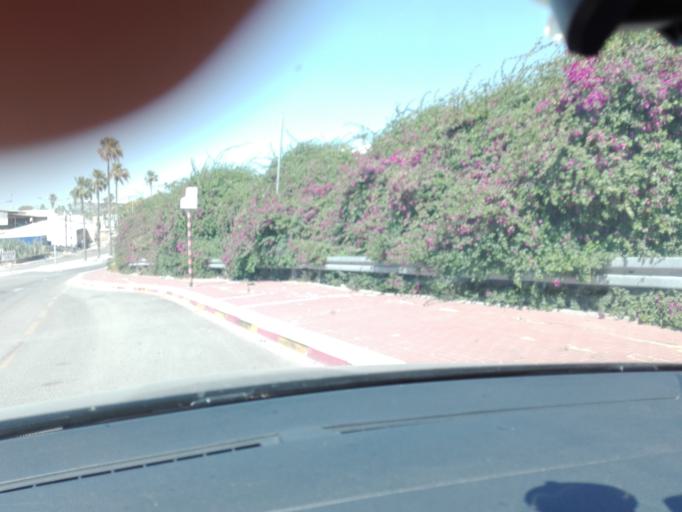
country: IL
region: Southern District
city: Qiryat Gat
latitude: 31.5982
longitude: 34.7771
